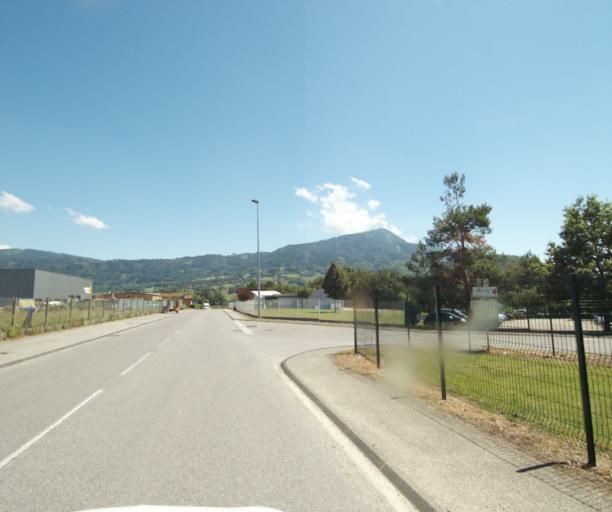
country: FR
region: Rhone-Alpes
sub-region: Departement de la Haute-Savoie
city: Ballaison
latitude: 46.2744
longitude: 6.3503
